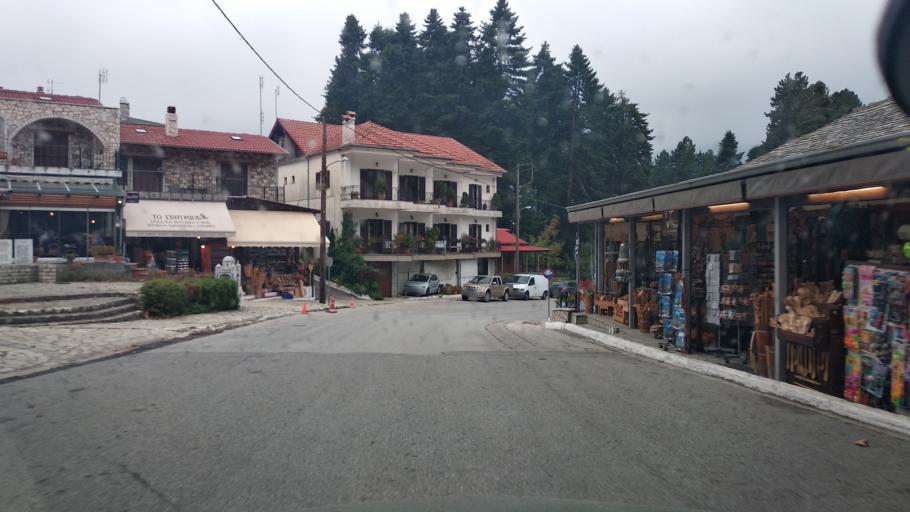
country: GR
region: Thessaly
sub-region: Trikala
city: Pyli
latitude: 39.5010
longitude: 21.5392
